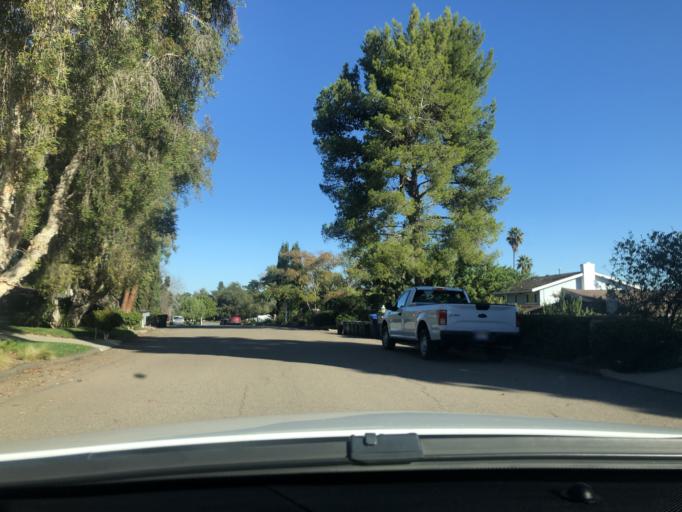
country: US
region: California
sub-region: San Diego County
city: Casa de Oro-Mount Helix
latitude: 32.7683
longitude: -116.9468
